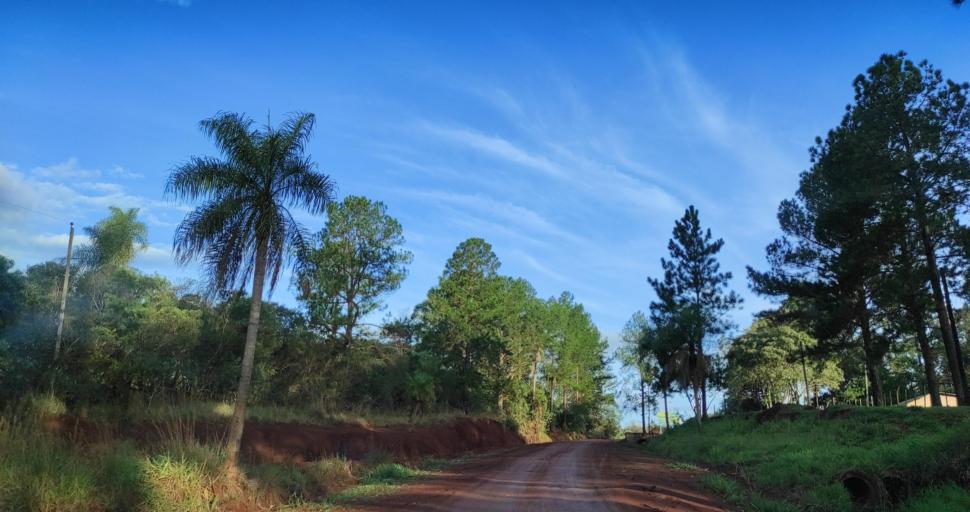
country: AR
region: Misiones
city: Garupa
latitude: -27.5128
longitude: -55.8544
